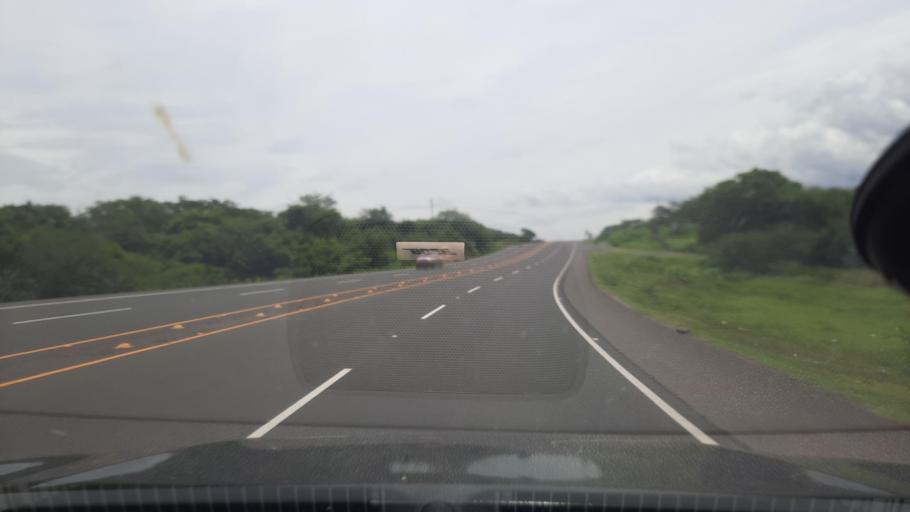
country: HN
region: Valle
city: Aramecina
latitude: 13.7189
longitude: -87.7106
